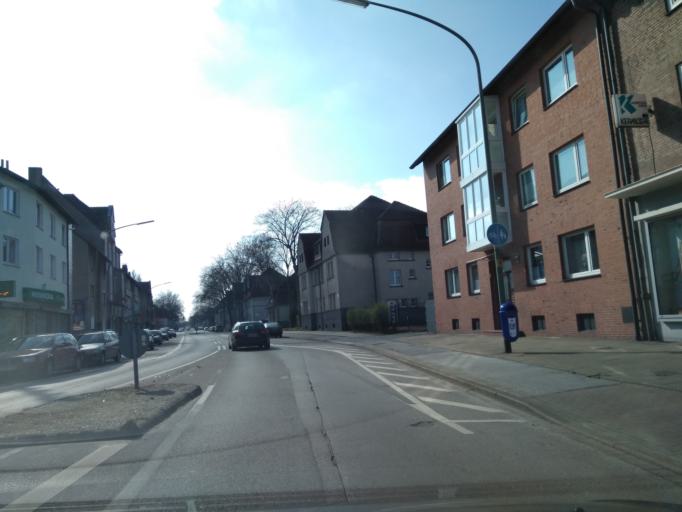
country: DE
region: North Rhine-Westphalia
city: Marl
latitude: 51.6061
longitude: 7.0488
